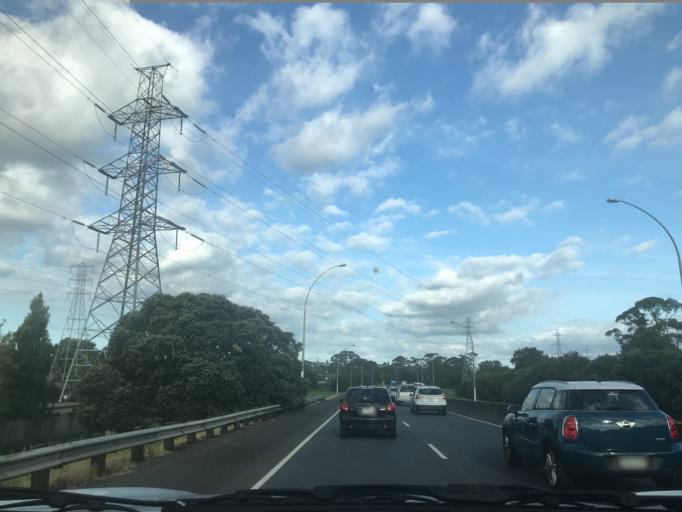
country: NZ
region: Auckland
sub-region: Auckland
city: Tamaki
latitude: -36.9136
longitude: 174.8626
